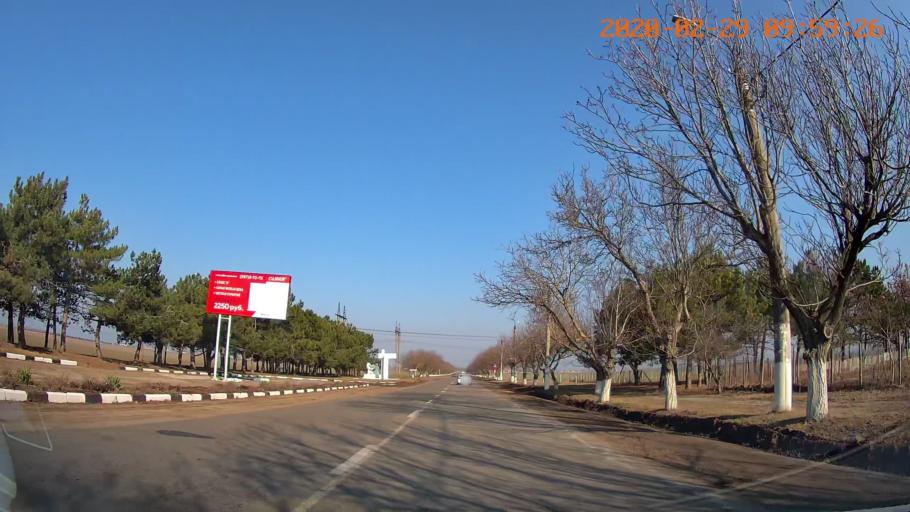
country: MD
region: Telenesti
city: Slobozia
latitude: 46.7569
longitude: 29.6884
